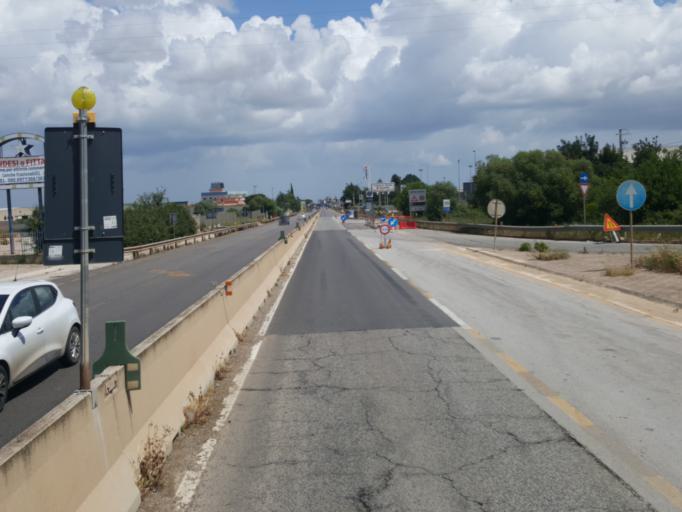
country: IT
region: Apulia
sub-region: Provincia di Bari
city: Bitetto
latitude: 41.0756
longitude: 16.7552
